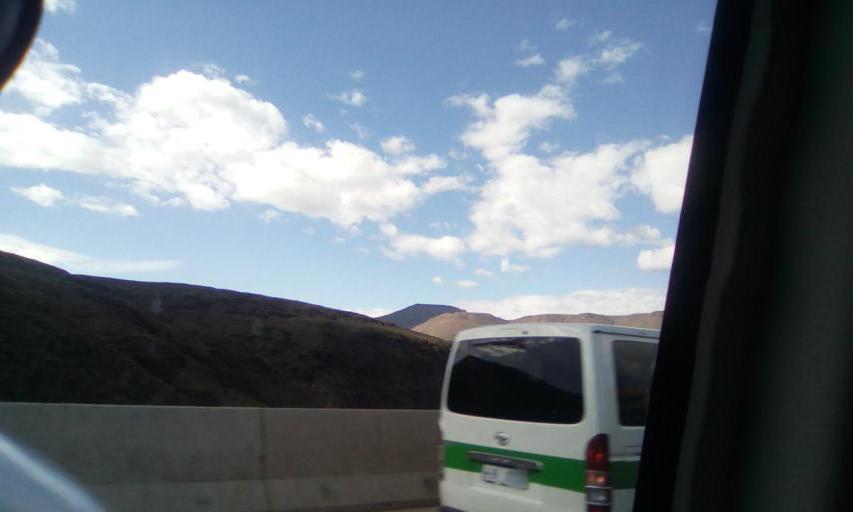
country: LS
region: Qacha's Nek
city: Qacha's Nek
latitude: -30.0237
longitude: 28.1820
